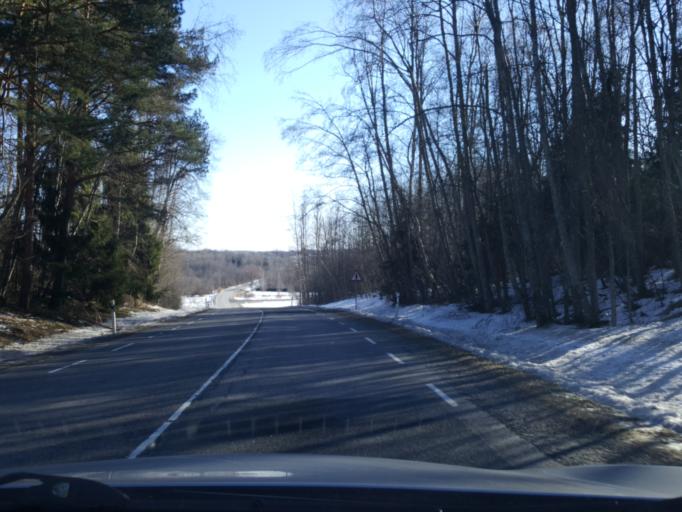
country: EE
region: Viljandimaa
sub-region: Vohma linn
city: Vohma
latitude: 58.5231
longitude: 25.6182
